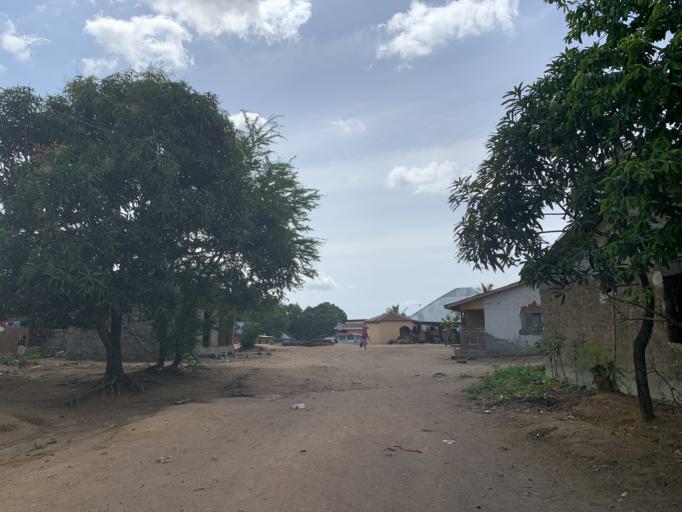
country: SL
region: Western Area
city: Waterloo
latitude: 8.3363
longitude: -13.0443
